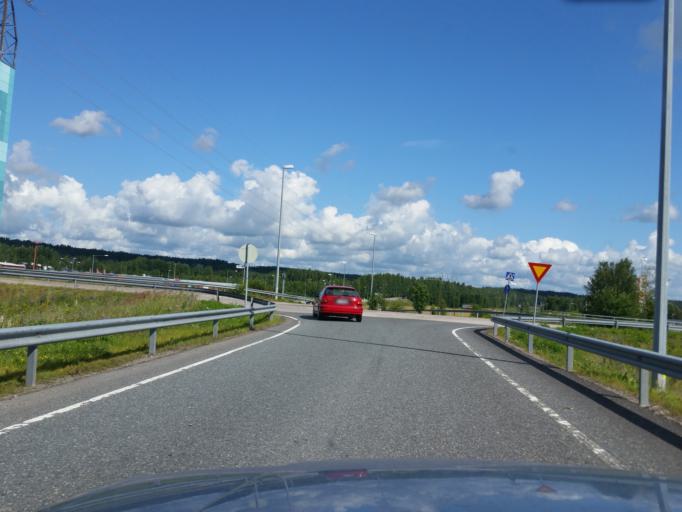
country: FI
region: Uusimaa
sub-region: Helsinki
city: Vihti
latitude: 60.3315
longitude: 24.3342
